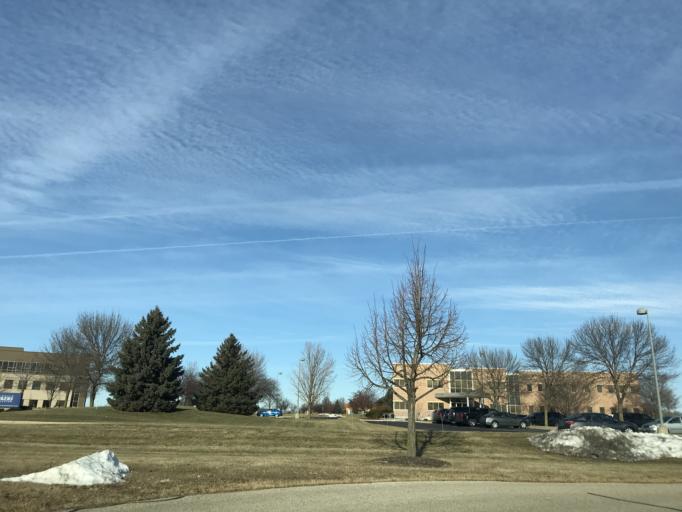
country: US
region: Wisconsin
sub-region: Dane County
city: Windsor
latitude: 43.1479
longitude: -89.2937
